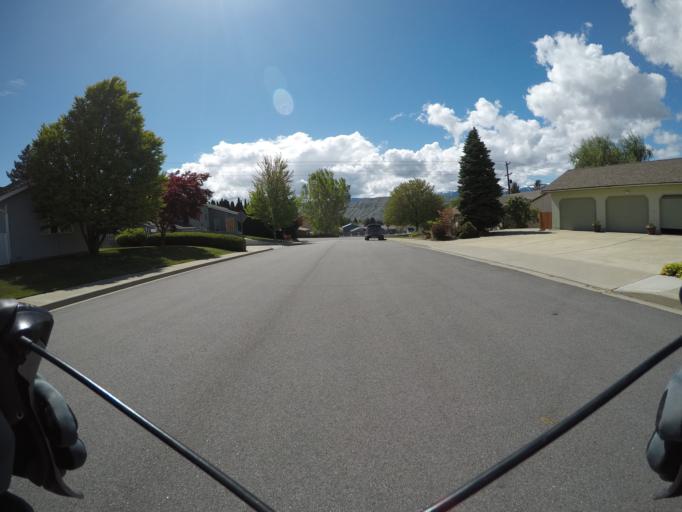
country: US
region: Washington
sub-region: Douglas County
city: East Wenatchee Bench
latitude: 47.4209
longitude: -120.2787
